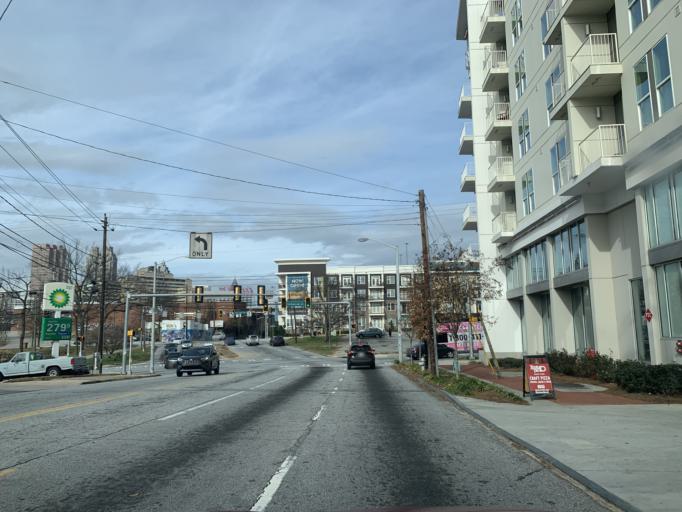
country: US
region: Georgia
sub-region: Fulton County
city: Atlanta
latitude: 33.7464
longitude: -84.3792
